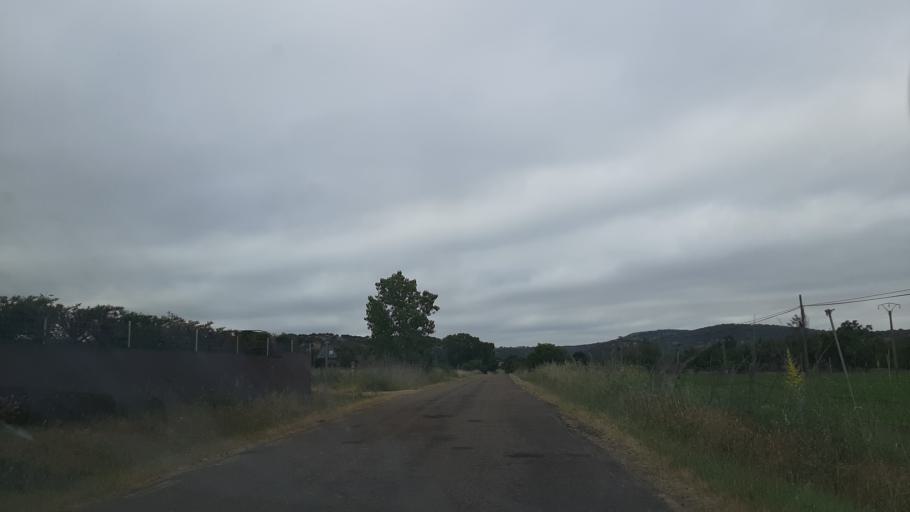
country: ES
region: Castille and Leon
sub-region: Provincia de Salamanca
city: Pastores
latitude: 40.5635
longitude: -6.4854
